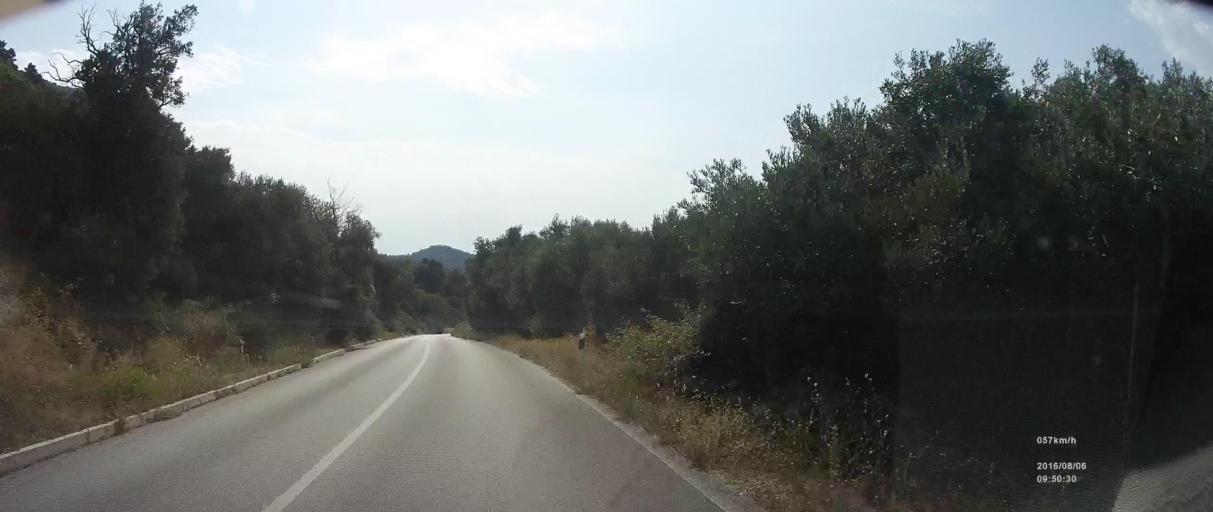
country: HR
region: Dubrovacko-Neretvanska
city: Blato
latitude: 42.7335
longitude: 17.5536
